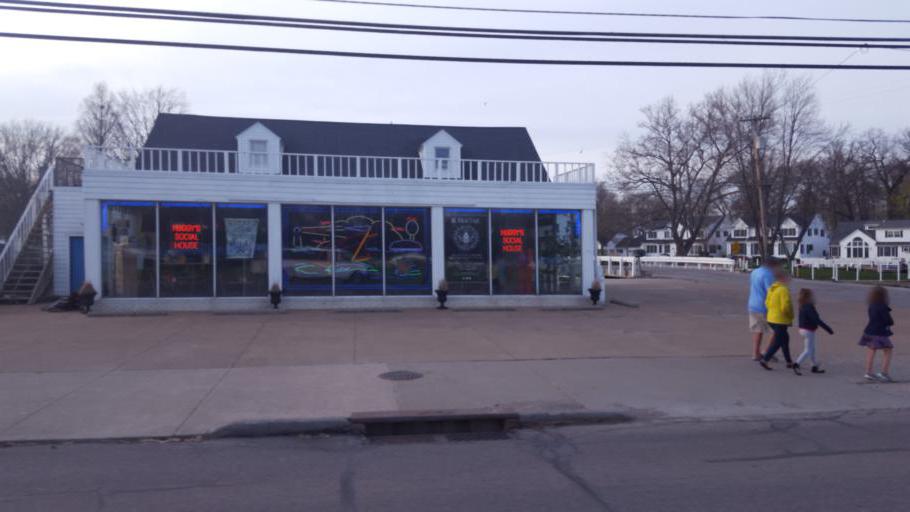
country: US
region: Ohio
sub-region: Lorain County
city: Vermilion
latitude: 41.4228
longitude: -82.3559
